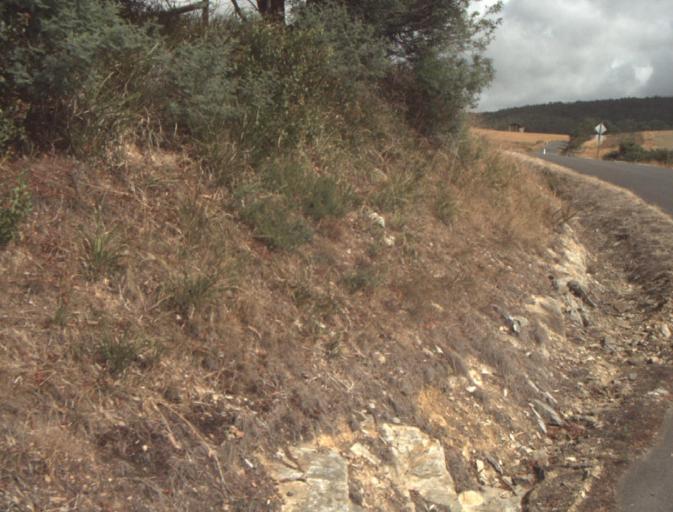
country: AU
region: Tasmania
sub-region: Northern Midlands
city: Evandale
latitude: -41.4784
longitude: 147.5004
